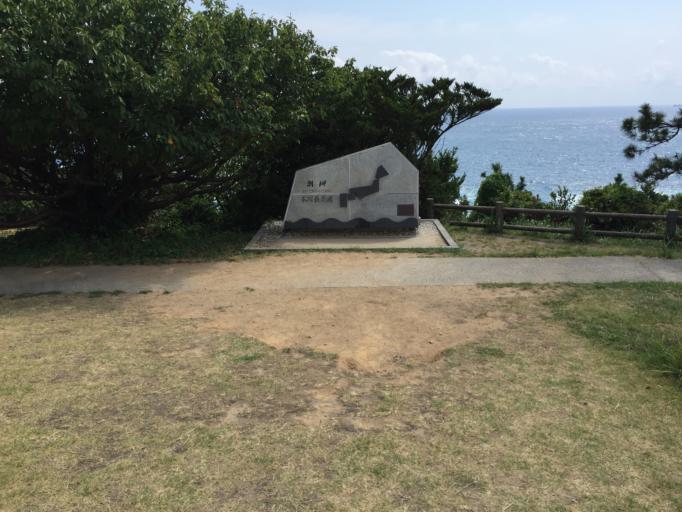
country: JP
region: Wakayama
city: Shingu
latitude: 33.4362
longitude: 135.7617
